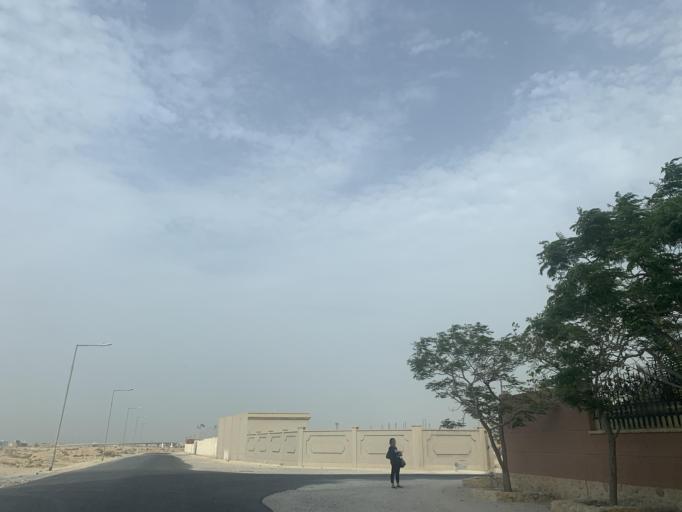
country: BH
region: Northern
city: Madinat `Isa
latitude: 26.1781
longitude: 50.4857
